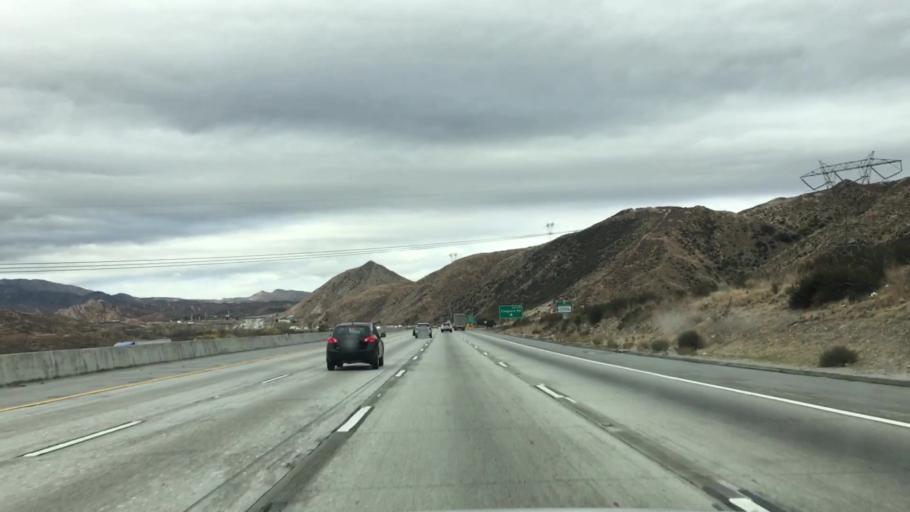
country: US
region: California
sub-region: San Bernardino County
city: Oak Hills
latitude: 34.2945
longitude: -117.4537
